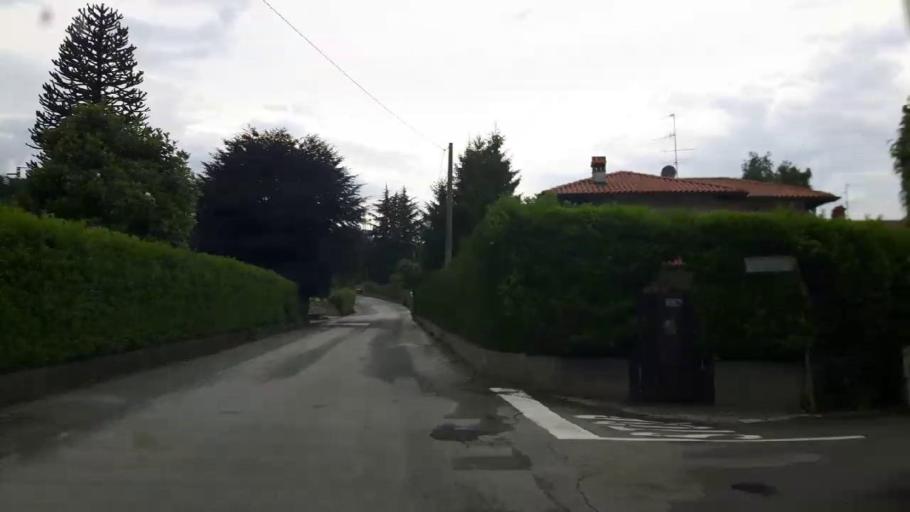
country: IT
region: Piedmont
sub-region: Provincia Verbano-Cusio-Ossola
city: Gignese
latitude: 45.8696
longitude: 8.5252
